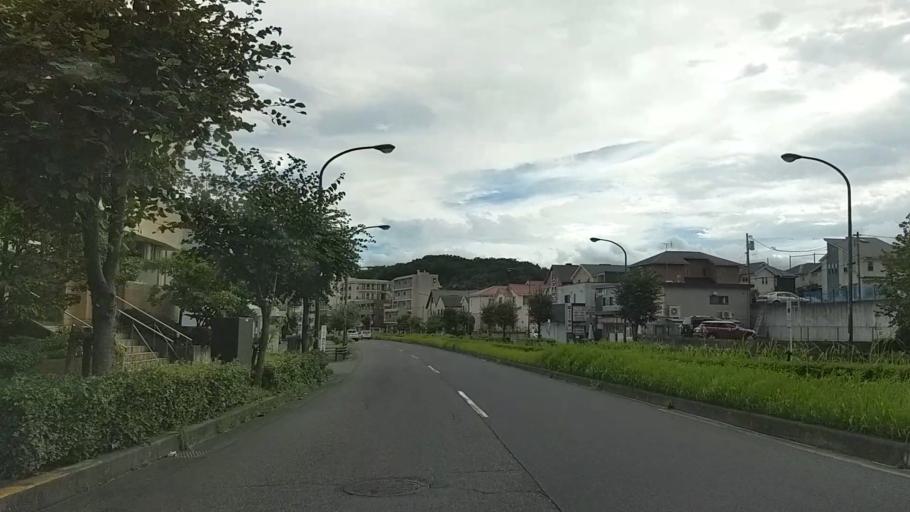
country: JP
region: Tokyo
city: Hachioji
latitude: 35.6291
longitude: 139.3276
